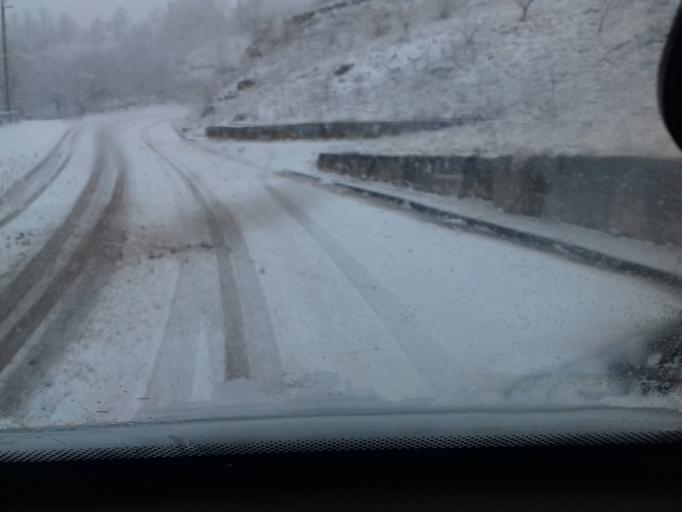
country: BA
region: Federation of Bosnia and Herzegovina
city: Lokvine
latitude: 44.2326
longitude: 17.8319
